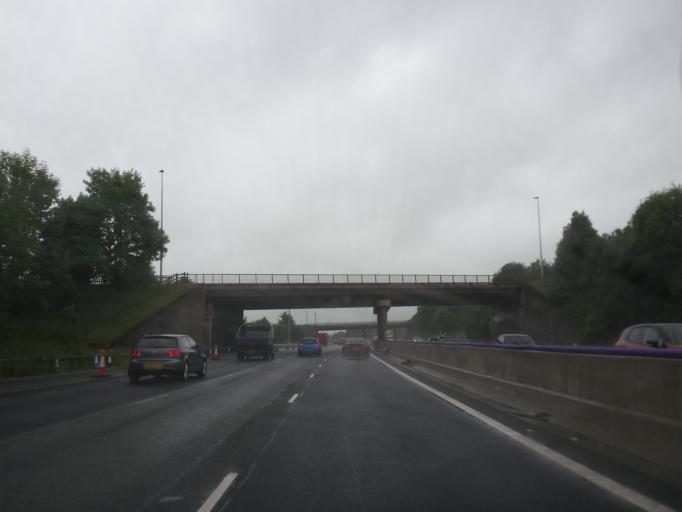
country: GB
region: England
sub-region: Derbyshire
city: Bolsover
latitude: 53.1991
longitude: -1.3223
